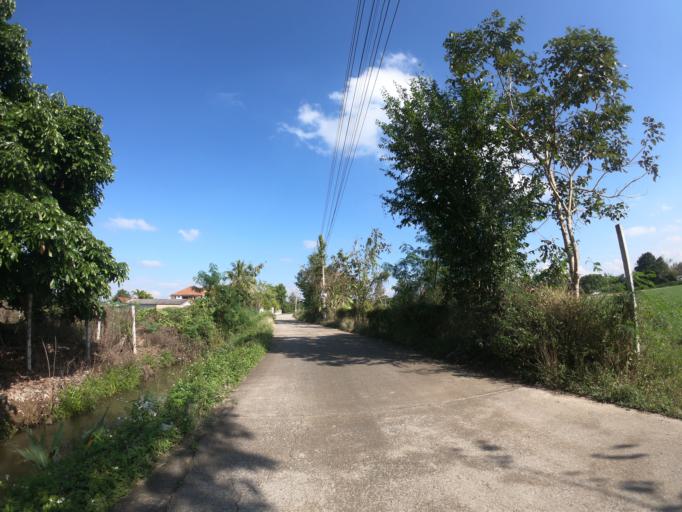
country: TH
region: Chiang Mai
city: Saraphi
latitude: 18.7139
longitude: 99.0114
